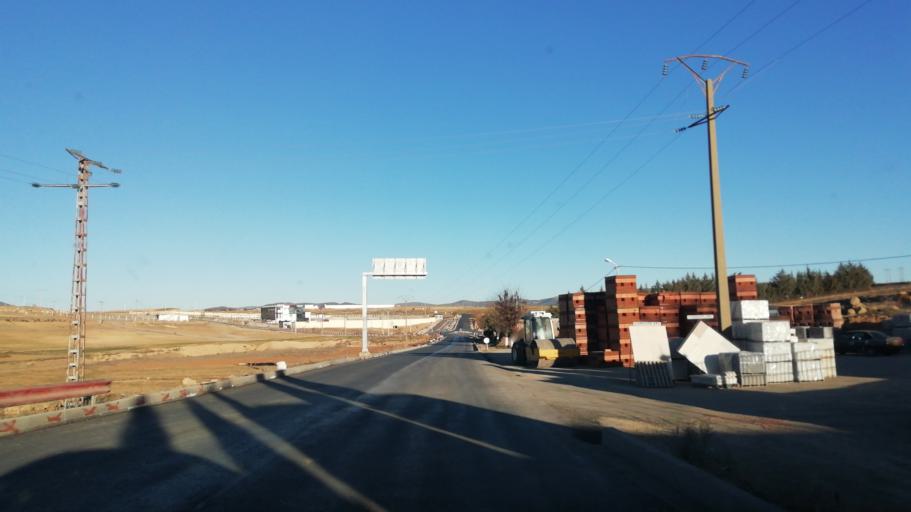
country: DZ
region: Tlemcen
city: Sebdou
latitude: 34.6551
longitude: -1.3129
